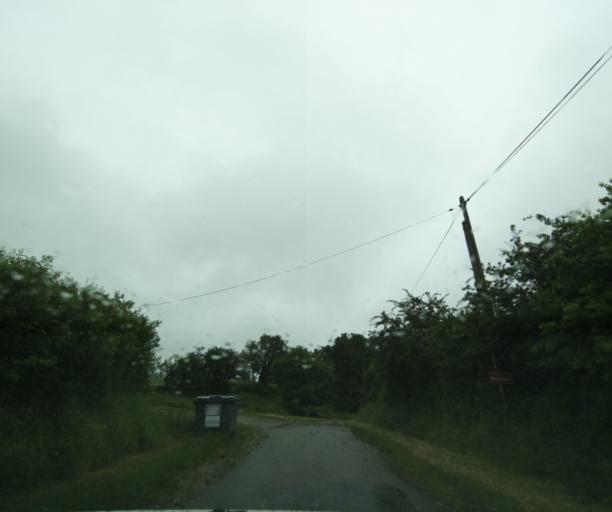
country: FR
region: Bourgogne
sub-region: Departement de Saone-et-Loire
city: Charolles
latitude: 46.4003
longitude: 4.2684
